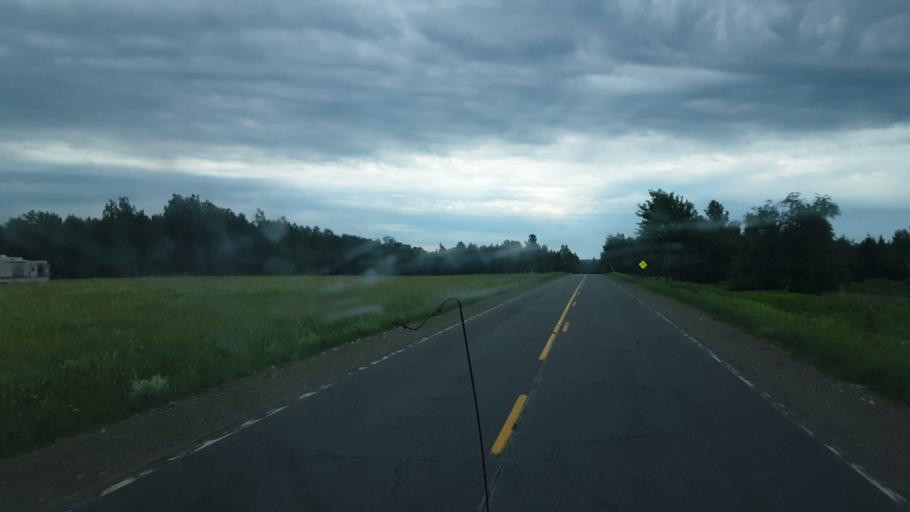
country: US
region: Maine
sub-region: Penobscot County
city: Medway
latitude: 45.7611
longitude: -68.3127
